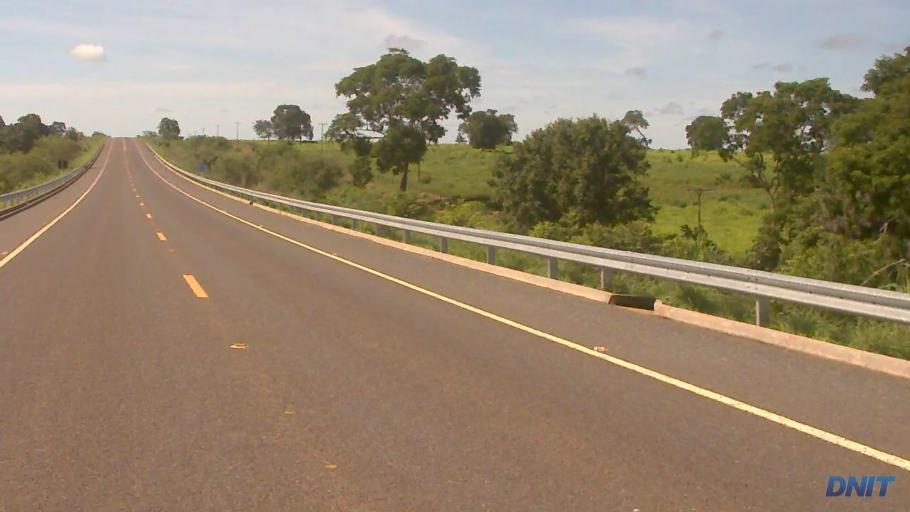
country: BR
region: Goias
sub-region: Sao Miguel Do Araguaia
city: Sao Miguel do Araguaia
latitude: -13.3627
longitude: -50.1460
